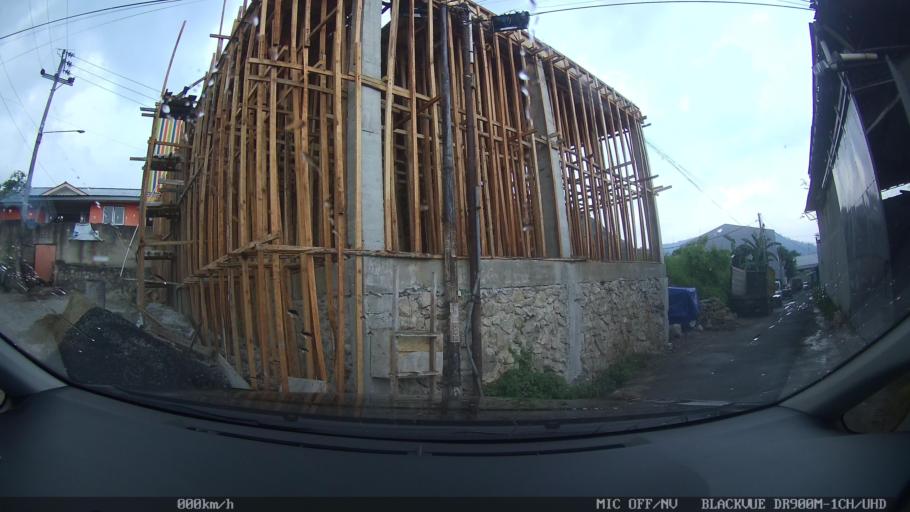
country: ID
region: Lampung
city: Bandarlampung
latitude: -5.4346
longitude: 105.2838
